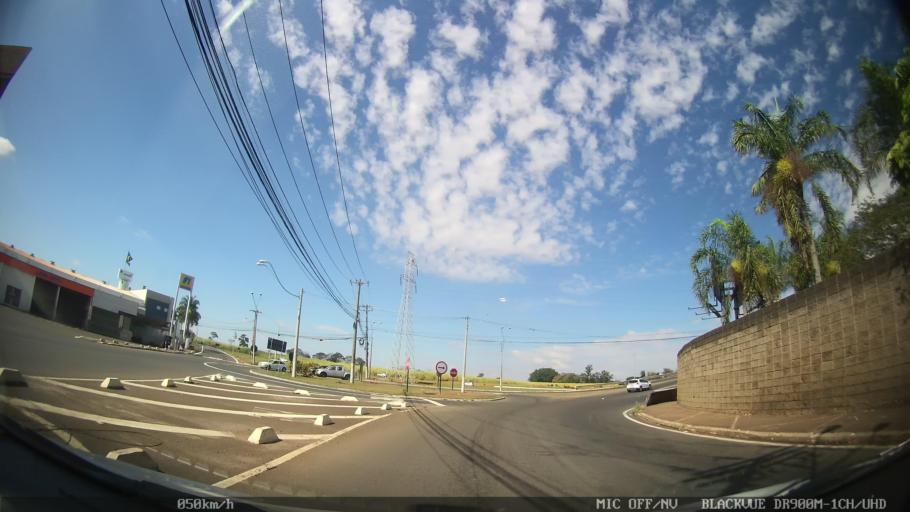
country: BR
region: Sao Paulo
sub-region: Nova Odessa
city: Nova Odessa
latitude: -22.7531
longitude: -47.2998
